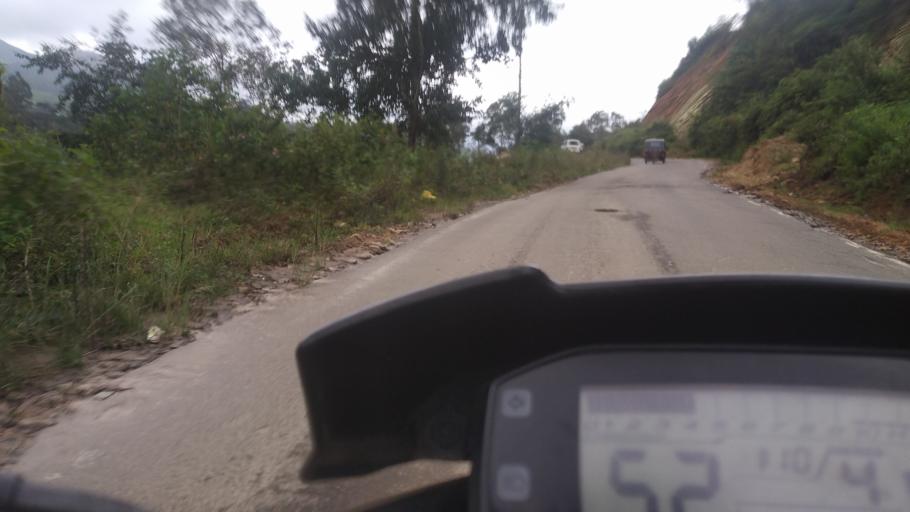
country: IN
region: Kerala
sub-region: Idukki
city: Munnar
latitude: 10.0838
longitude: 77.0676
